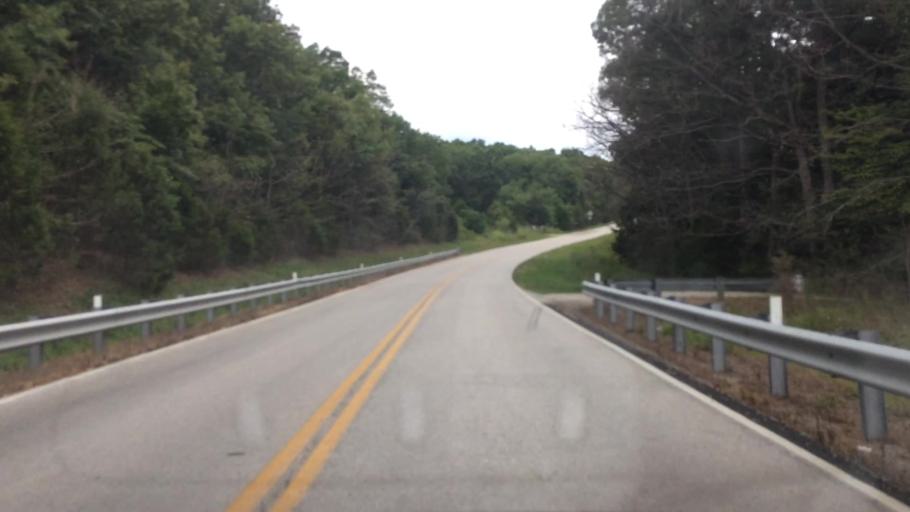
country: US
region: Missouri
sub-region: Webster County
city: Marshfield
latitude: 37.3036
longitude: -93.0019
